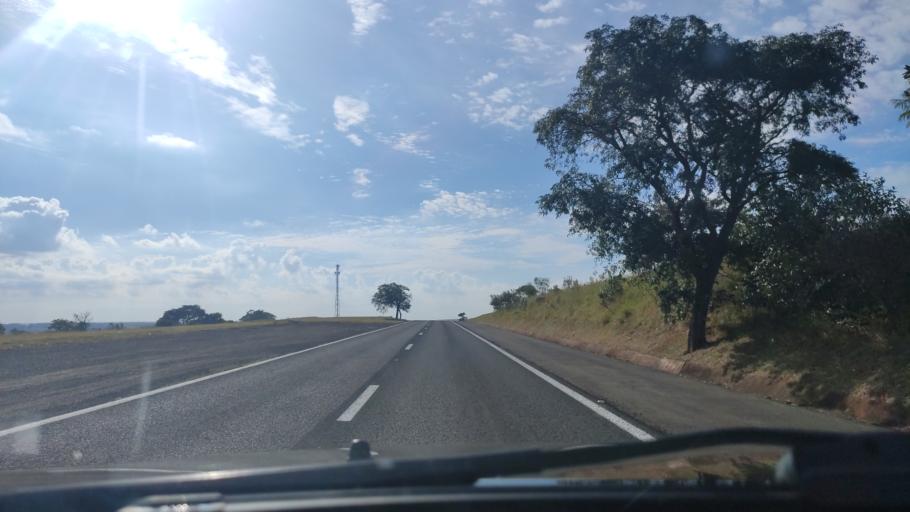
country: BR
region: Sao Paulo
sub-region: Avare
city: Avare
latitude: -22.9665
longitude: -48.8085
